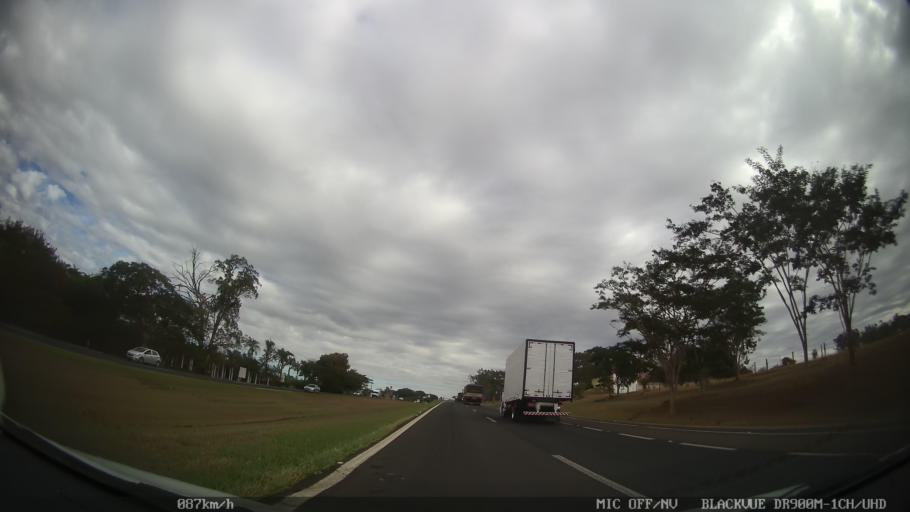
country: BR
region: Sao Paulo
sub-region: Sao Jose Do Rio Preto
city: Sao Jose do Rio Preto
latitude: -20.8136
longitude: -49.4754
